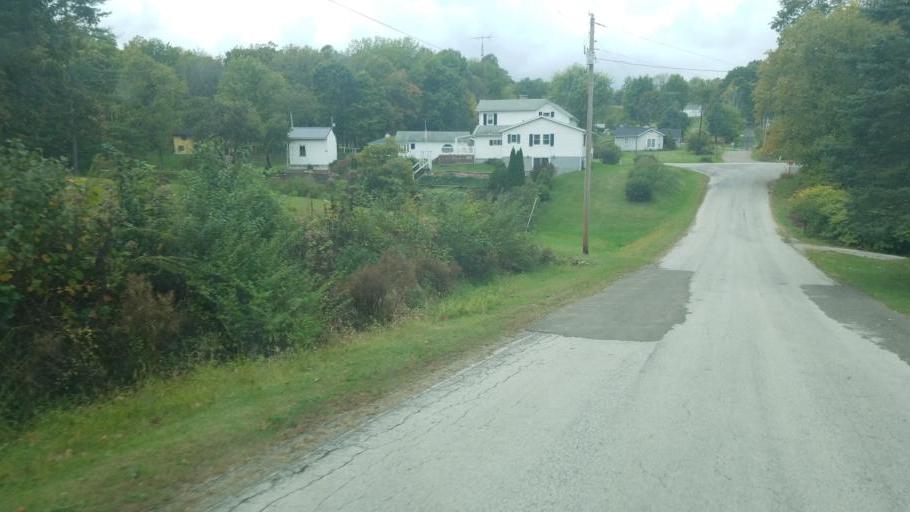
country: US
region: Ohio
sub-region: Wayne County
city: Shreve
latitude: 40.5794
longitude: -82.1086
